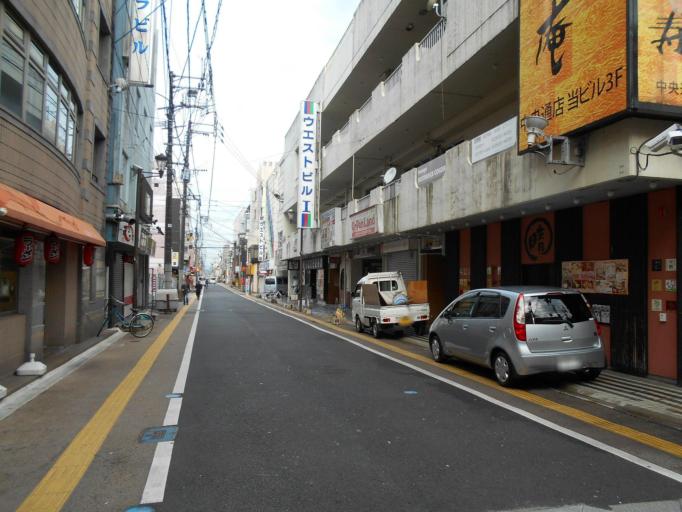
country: JP
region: Miyazaki
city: Miyazaki-shi
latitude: 31.9152
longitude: 131.4210
